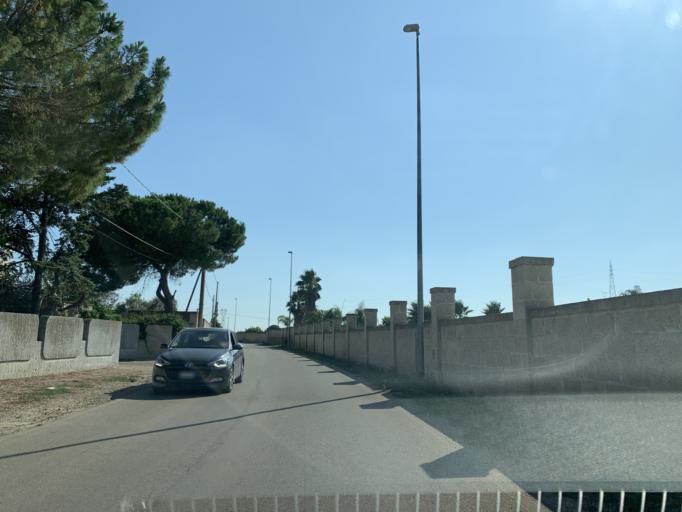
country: IT
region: Apulia
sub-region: Provincia di Lecce
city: Copertino
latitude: 40.2680
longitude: 18.0351
